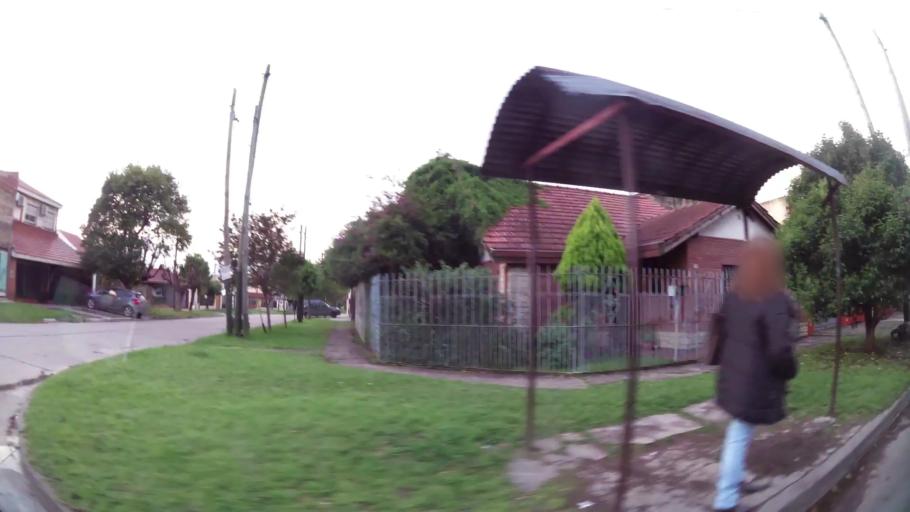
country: AR
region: Buenos Aires
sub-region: Partido de Lomas de Zamora
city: Lomas de Zamora
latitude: -34.7582
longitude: -58.3716
